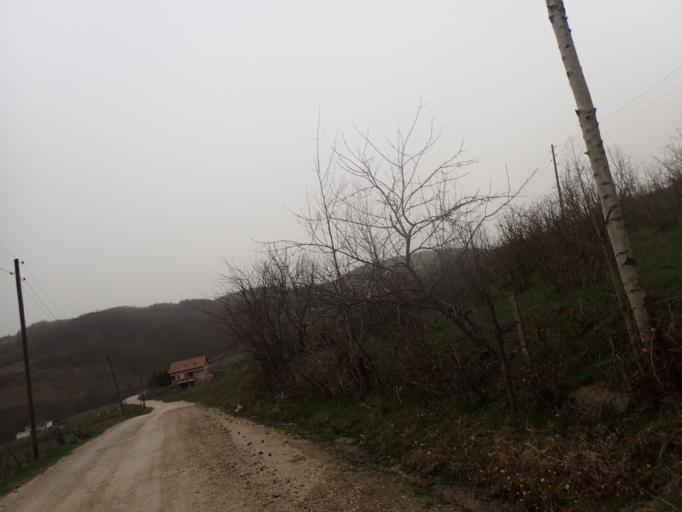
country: TR
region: Ordu
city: Kumru
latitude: 40.8210
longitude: 37.1853
